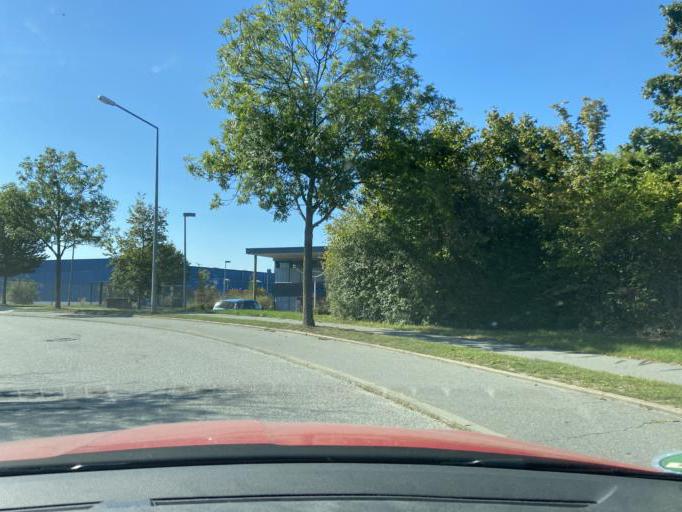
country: DE
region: Saxony
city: Ottendorf-Okrilla
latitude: 51.1842
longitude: 13.8359
